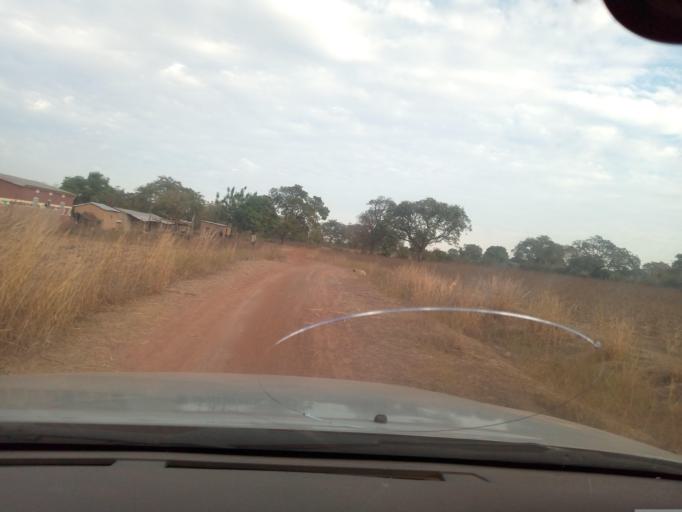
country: ML
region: Sikasso
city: Kadiolo
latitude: 10.5842
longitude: -5.8466
